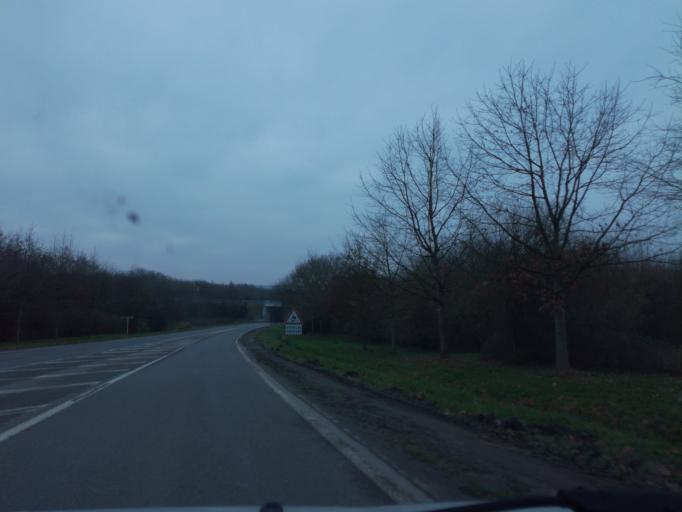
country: FR
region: Brittany
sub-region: Departement d'Ille-et-Vilaine
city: Gosne
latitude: 48.2424
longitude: -1.4609
